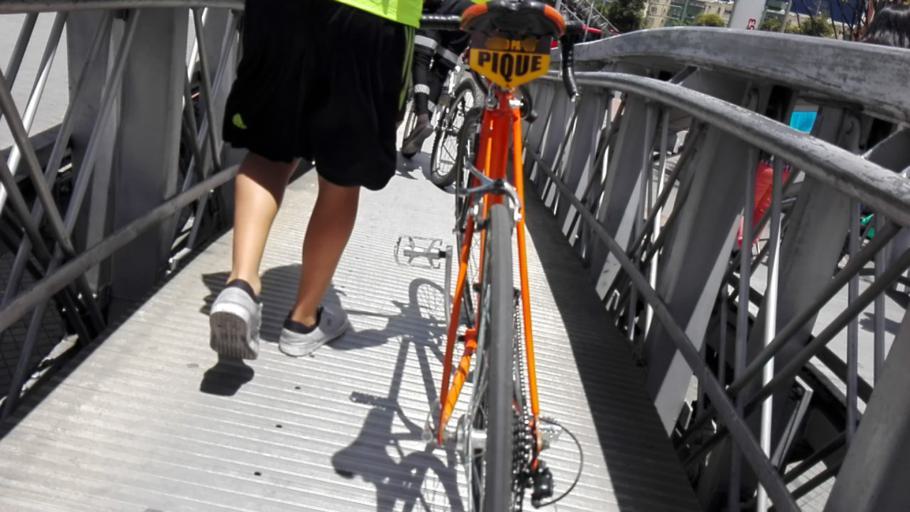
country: CO
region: Bogota D.C.
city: Barrio San Luis
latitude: 4.6822
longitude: -74.0782
